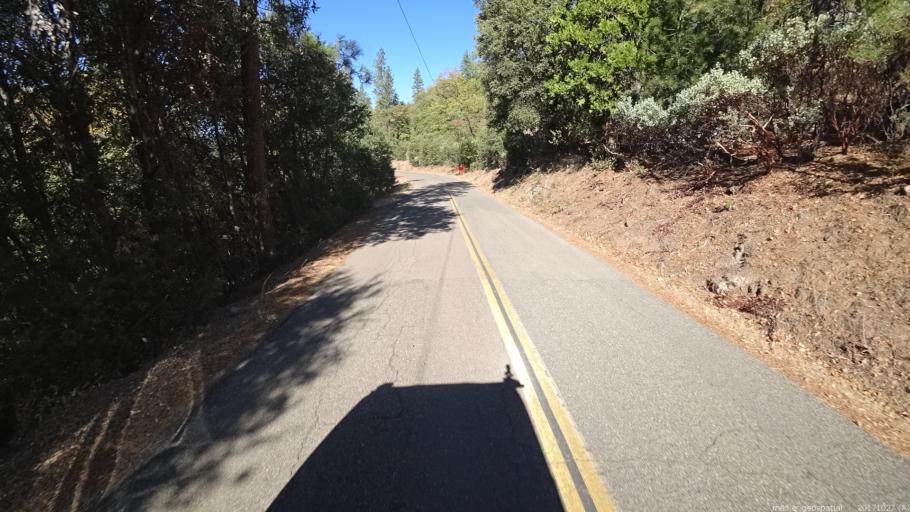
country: US
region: California
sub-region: Shasta County
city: Shingletown
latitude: 40.6638
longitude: -121.8834
